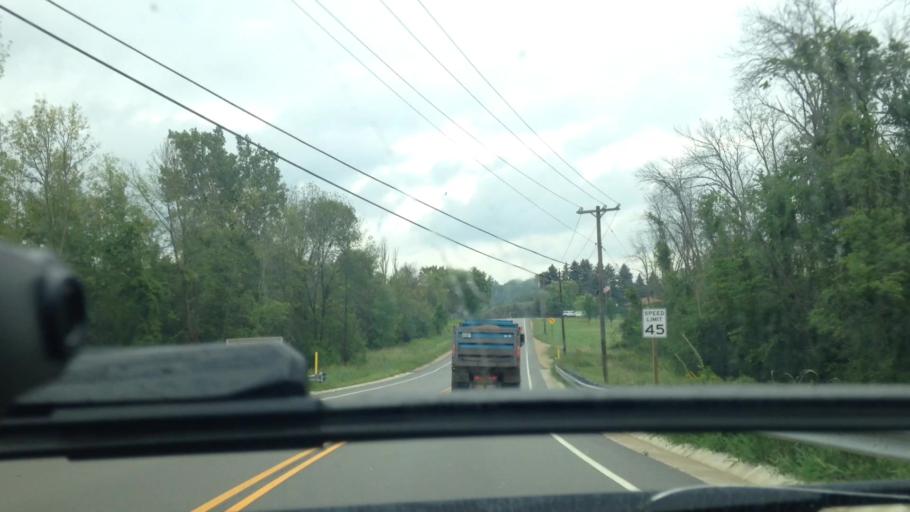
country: US
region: Wisconsin
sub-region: Washington County
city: Richfield
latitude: 43.2190
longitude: -88.1722
